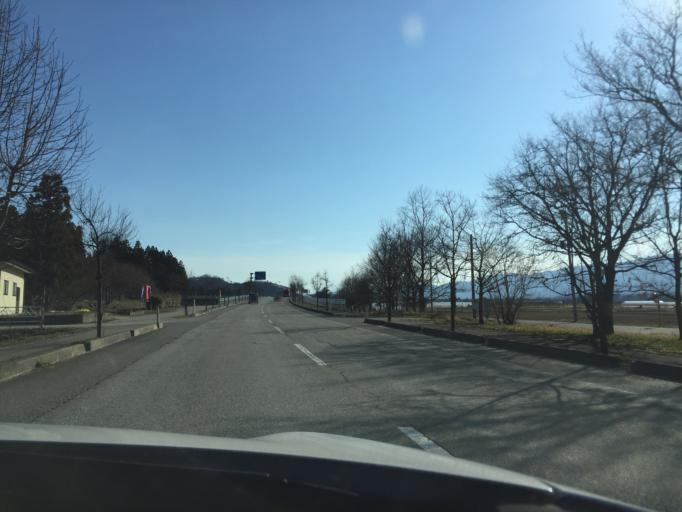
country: JP
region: Yamagata
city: Nagai
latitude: 38.1734
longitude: 140.0921
